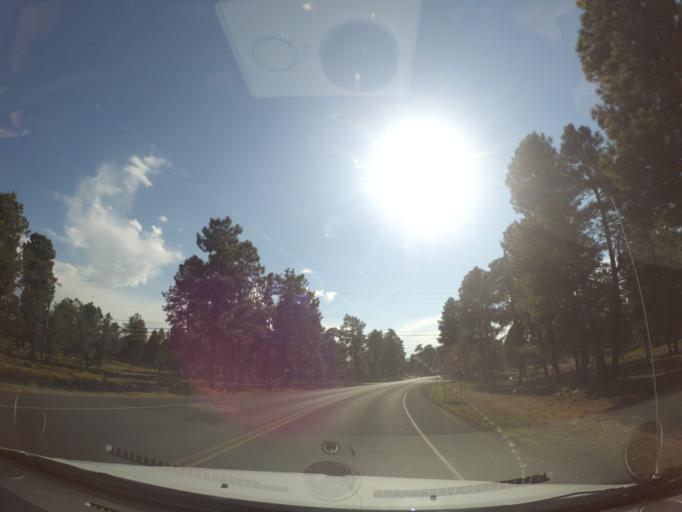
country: US
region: Arizona
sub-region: Coconino County
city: Grand Canyon
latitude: 36.0552
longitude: -112.1183
